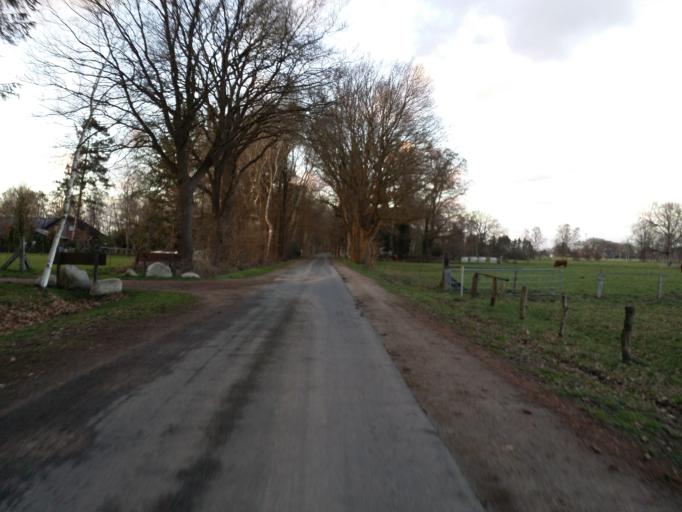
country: DE
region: Lower Saxony
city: Gross Ippener
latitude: 52.9918
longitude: 8.6017
